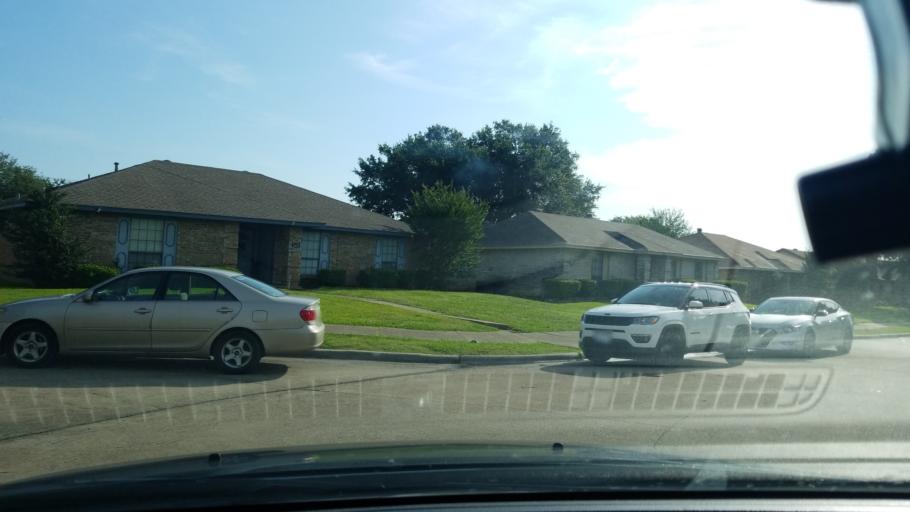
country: US
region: Texas
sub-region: Dallas County
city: Mesquite
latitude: 32.8045
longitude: -96.6144
